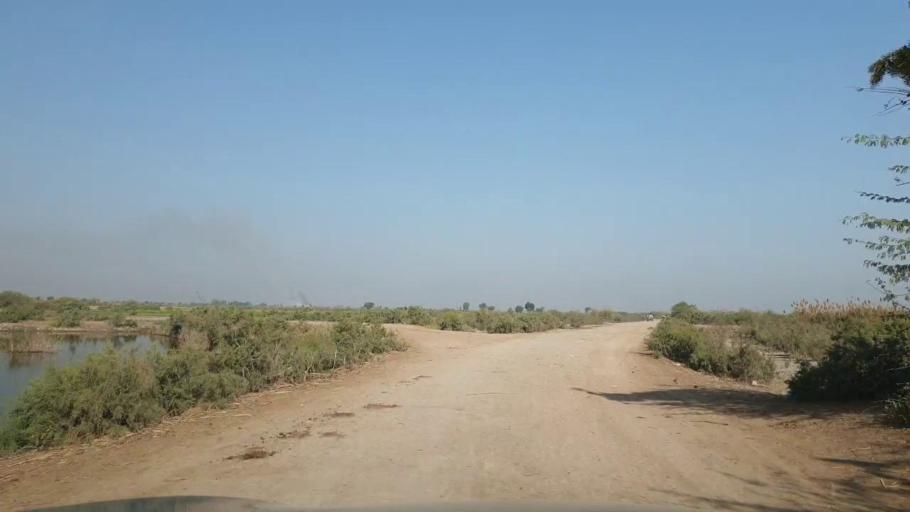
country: PK
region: Sindh
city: Mirpur Khas
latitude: 25.6488
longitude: 68.9090
